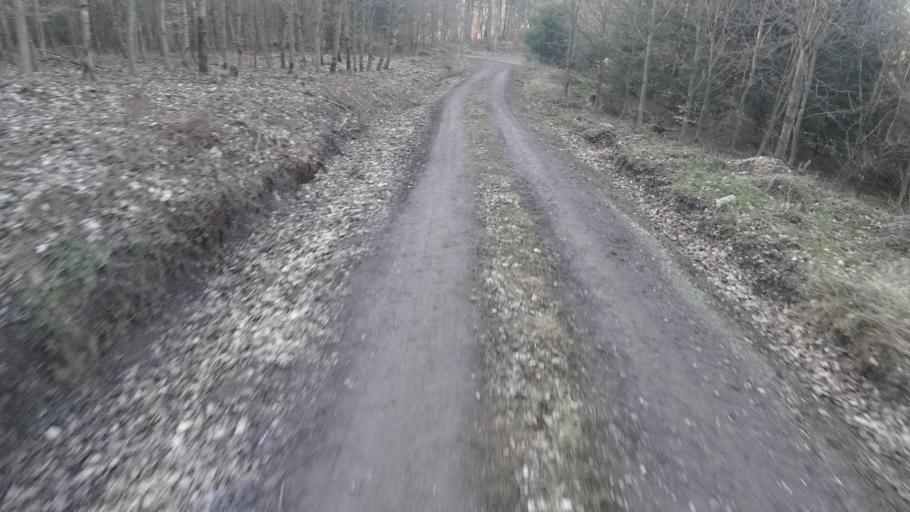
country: DE
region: Rheinland-Pfalz
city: Boppard
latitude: 50.2044
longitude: 7.5902
